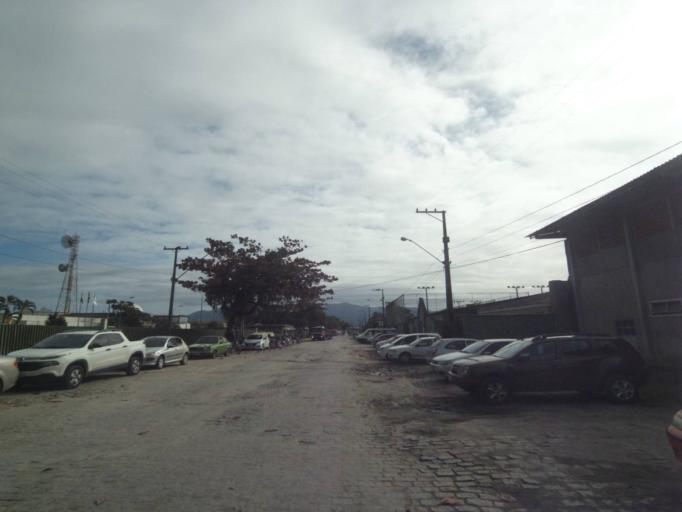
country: BR
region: Parana
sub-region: Paranagua
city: Paranagua
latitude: -25.5076
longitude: -48.5335
